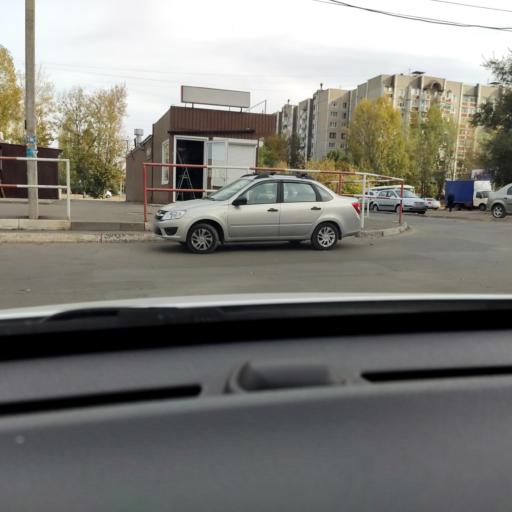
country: RU
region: Voronezj
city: Podgornoye
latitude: 51.7166
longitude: 39.1606
